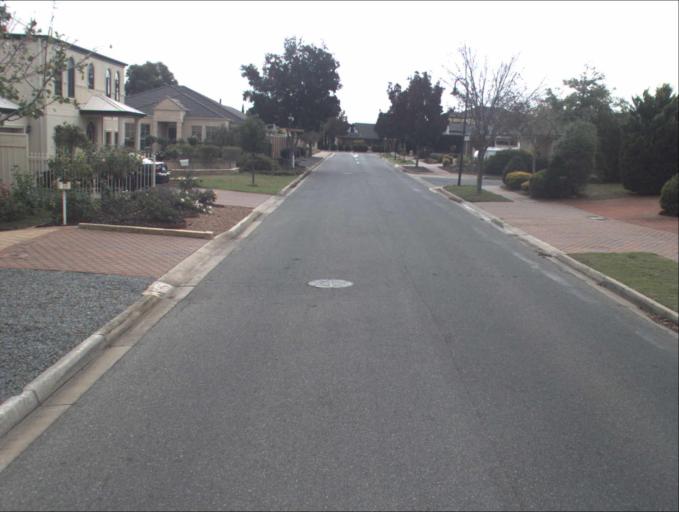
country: AU
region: South Australia
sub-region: Port Adelaide Enfield
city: Gilles Plains
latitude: -34.8565
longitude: 138.6304
